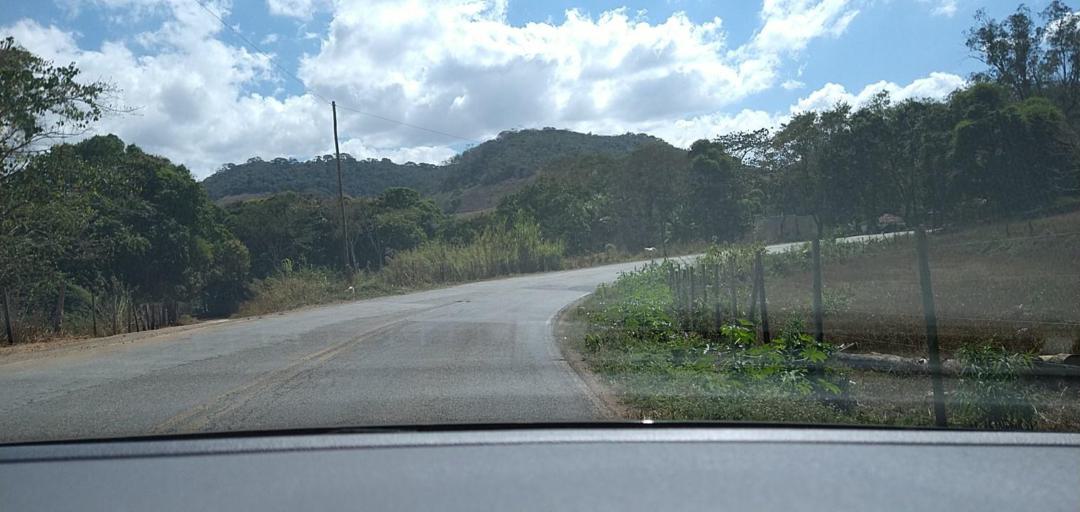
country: BR
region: Minas Gerais
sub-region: Ponte Nova
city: Ponte Nova
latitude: -20.2798
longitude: -42.9030
